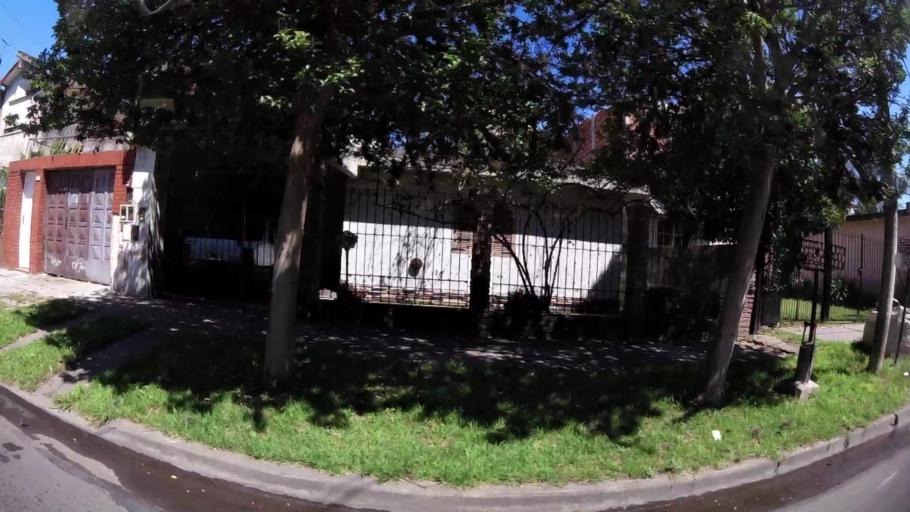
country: AR
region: Buenos Aires
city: Ituzaingo
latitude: -34.6668
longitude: -58.6601
